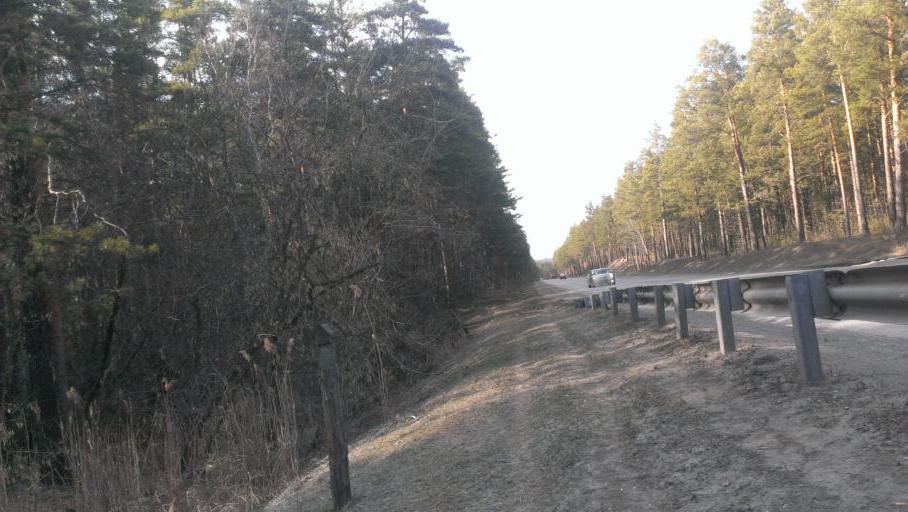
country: RU
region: Altai Krai
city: Yuzhnyy
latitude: 53.2923
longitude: 83.7071
